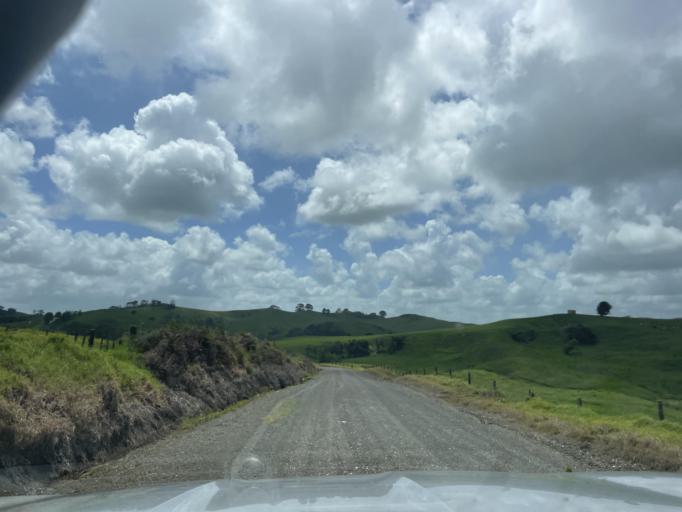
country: NZ
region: Auckland
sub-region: Auckland
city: Wellsford
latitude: -36.1957
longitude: 174.3355
